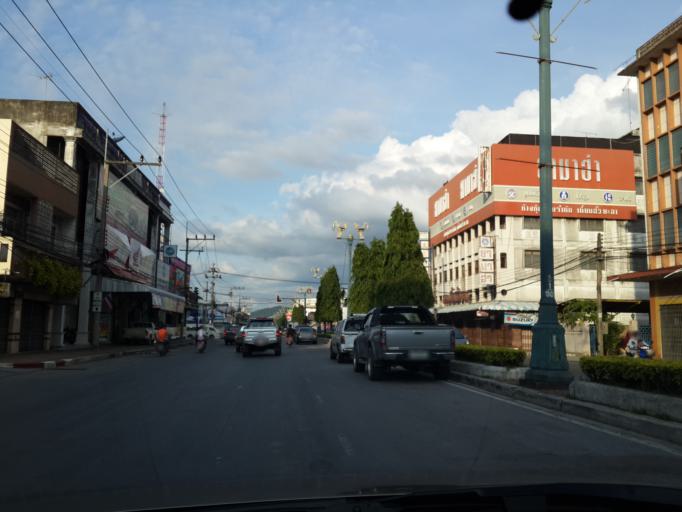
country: TH
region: Yala
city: Yala
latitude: 6.5578
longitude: 101.2878
